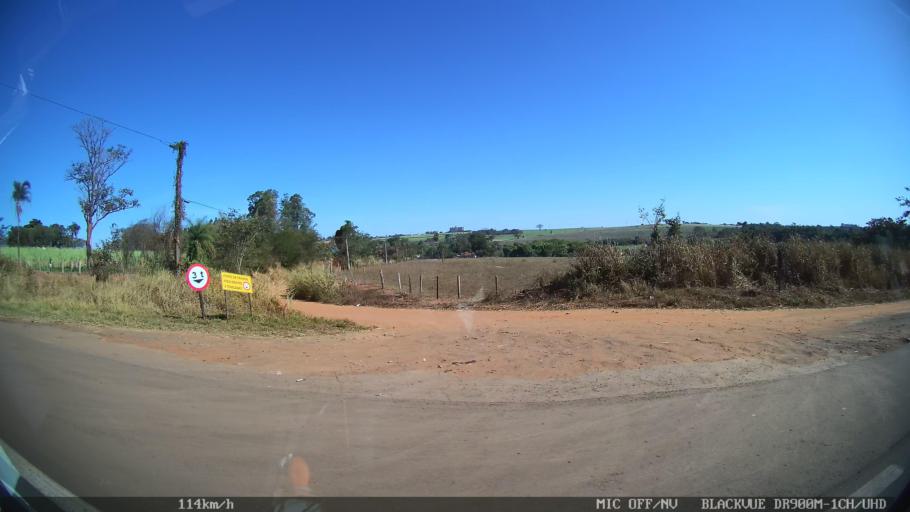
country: BR
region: Sao Paulo
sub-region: Olimpia
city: Olimpia
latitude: -20.6978
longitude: -48.8919
